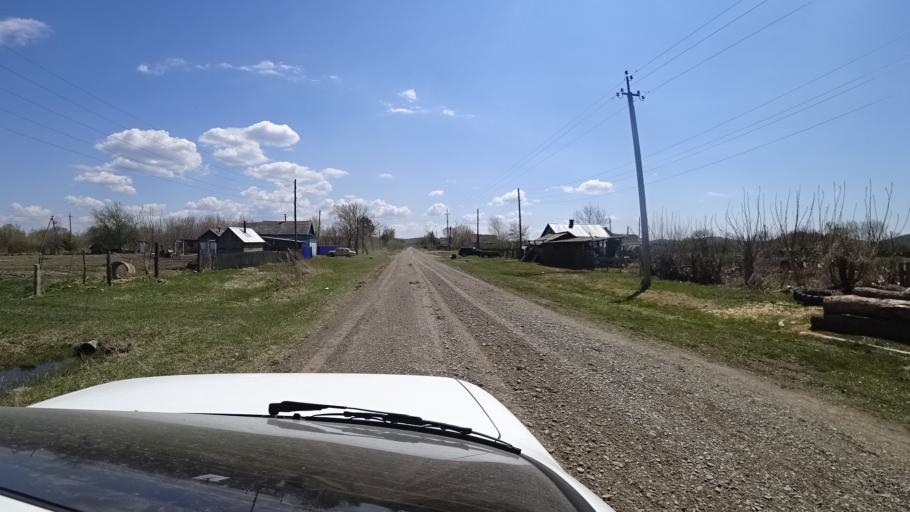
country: RU
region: Primorskiy
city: Lazo
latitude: 45.8016
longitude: 133.7626
